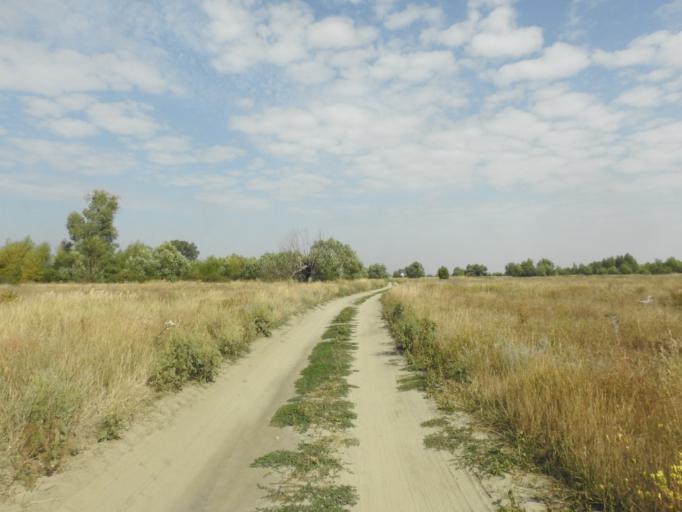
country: RU
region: Volgograd
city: Zhirnovsk
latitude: 51.2376
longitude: 44.9992
